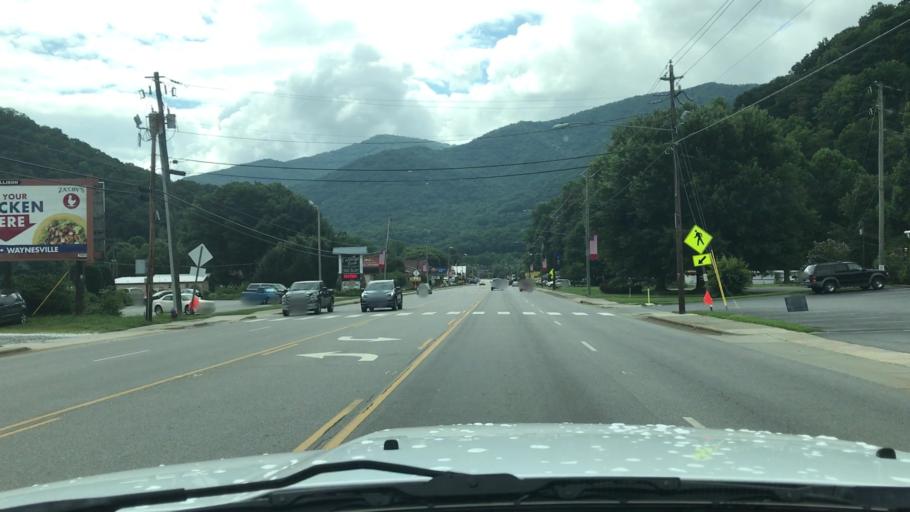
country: US
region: North Carolina
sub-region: Haywood County
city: Maggie Valley
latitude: 35.5161
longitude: -83.0859
